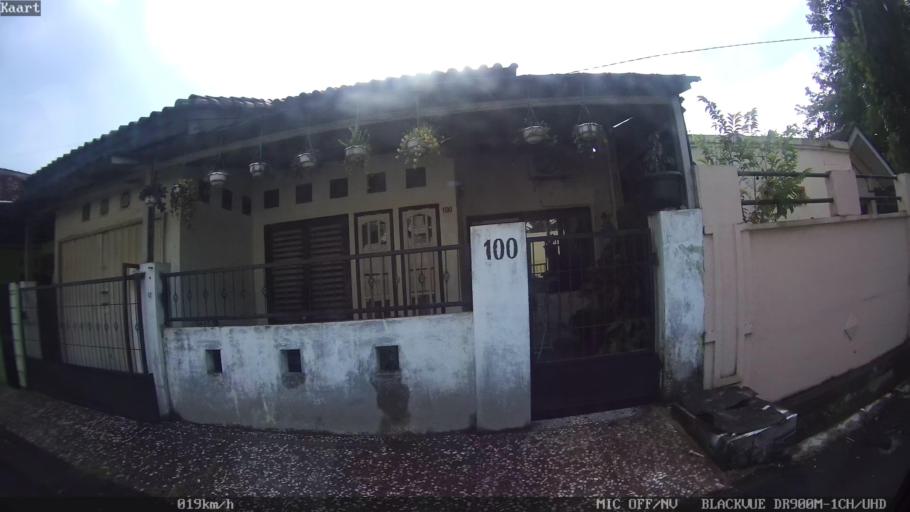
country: ID
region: Lampung
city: Kedaton
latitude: -5.3860
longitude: 105.3017
